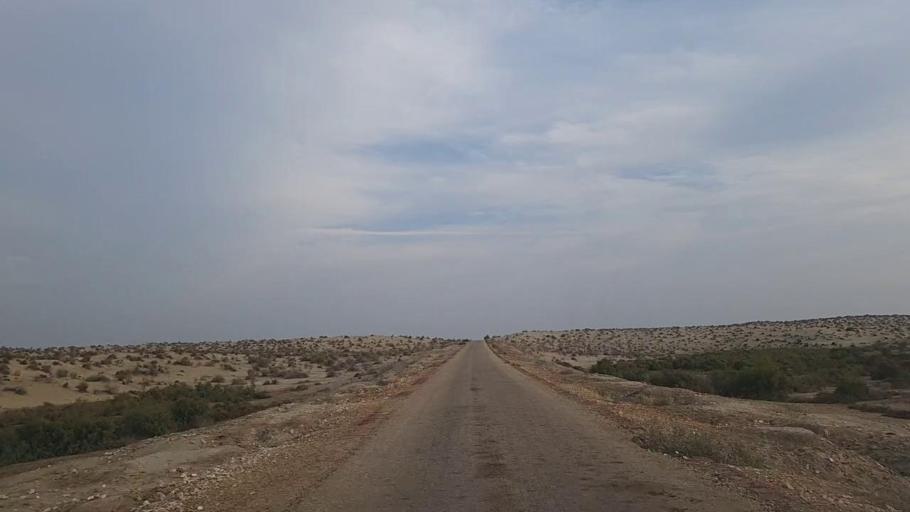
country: PK
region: Sindh
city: Daur
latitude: 26.5101
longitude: 68.5085
